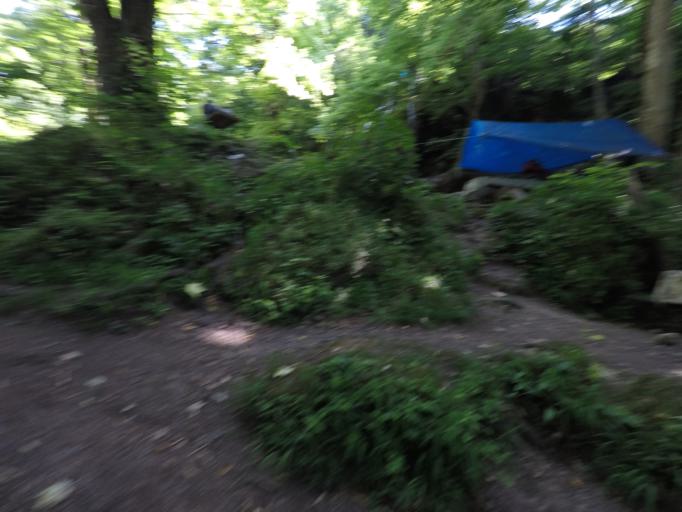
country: AZ
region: Qakh Rayon
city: Cinarli
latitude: 41.4931
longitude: 46.8589
